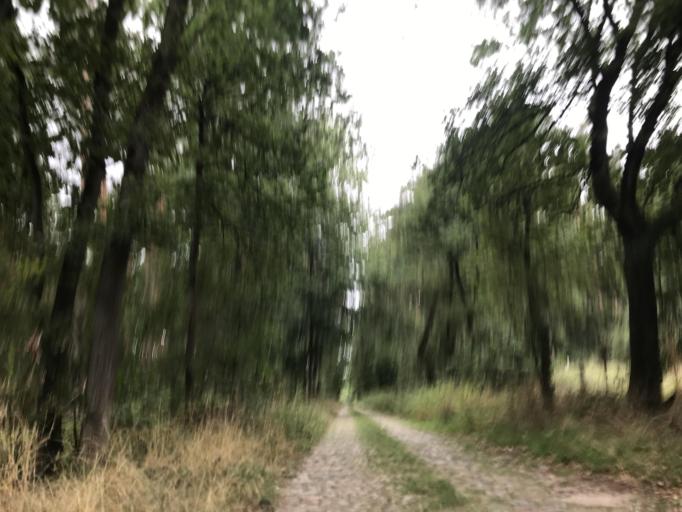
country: DE
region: Lower Saxony
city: Reinstorf
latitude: 53.2457
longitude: 10.5536
